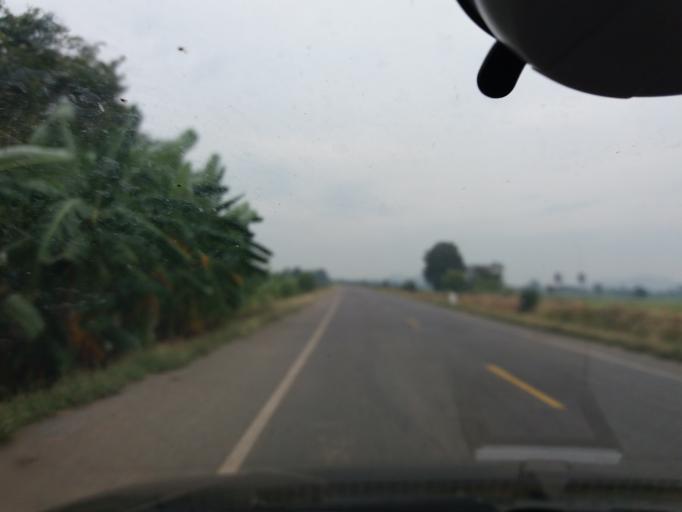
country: TH
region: Suphan Buri
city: Doem Bang Nang Buat
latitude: 14.8629
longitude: 100.1297
